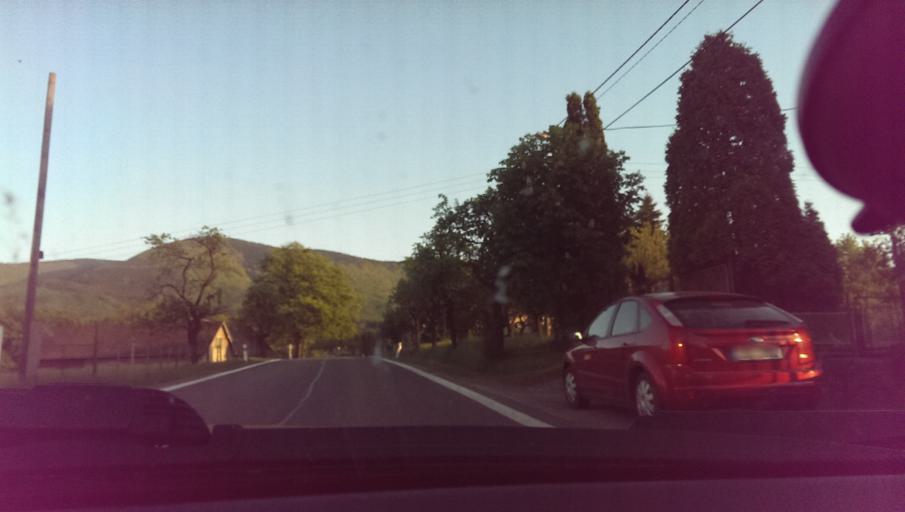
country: CZ
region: Moravskoslezsky
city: Frenstat pod Radhostem
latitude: 49.5240
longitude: 18.2035
